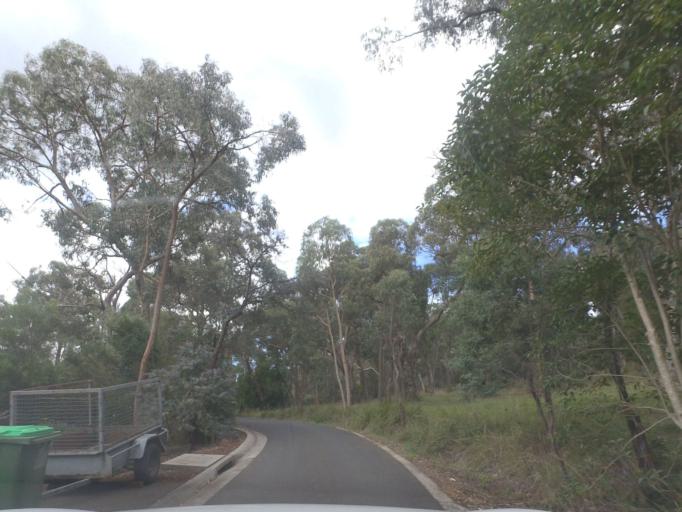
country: AU
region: Victoria
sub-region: Yarra Ranges
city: Montrose
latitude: -37.8304
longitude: 145.3390
